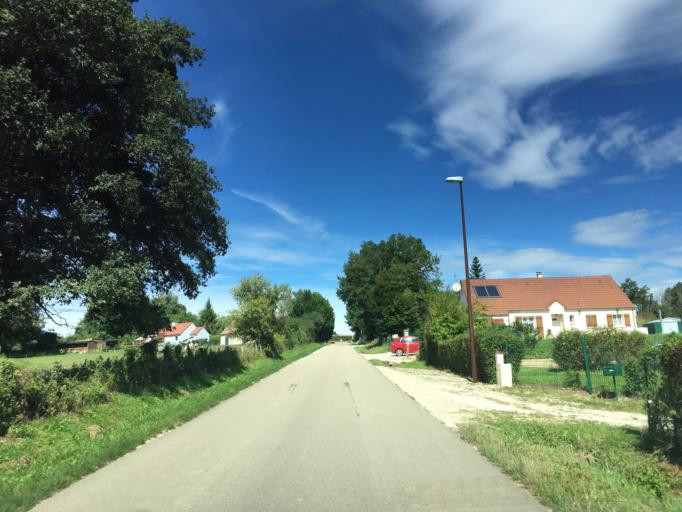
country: FR
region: Bourgogne
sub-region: Departement de l'Yonne
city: Charbuy
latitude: 47.8170
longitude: 3.4782
